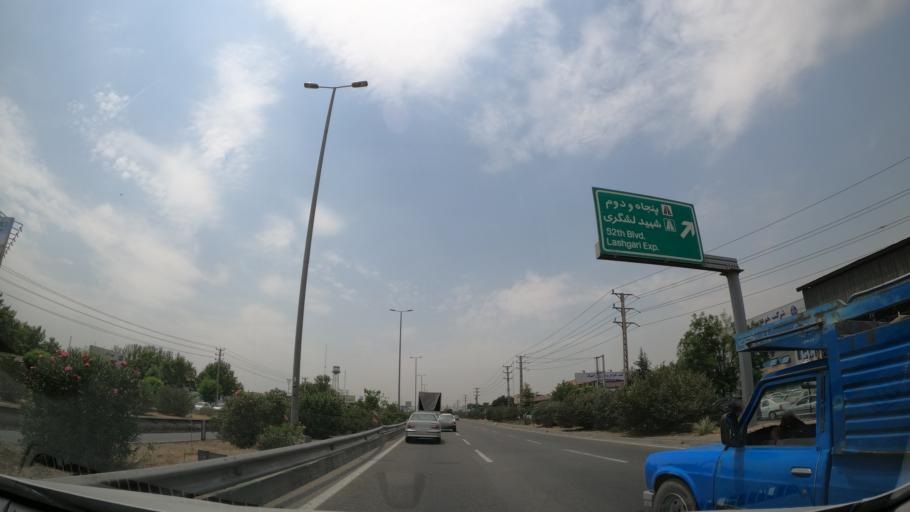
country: IR
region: Tehran
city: Shahr-e Qods
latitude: 35.7063
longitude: 51.1731
